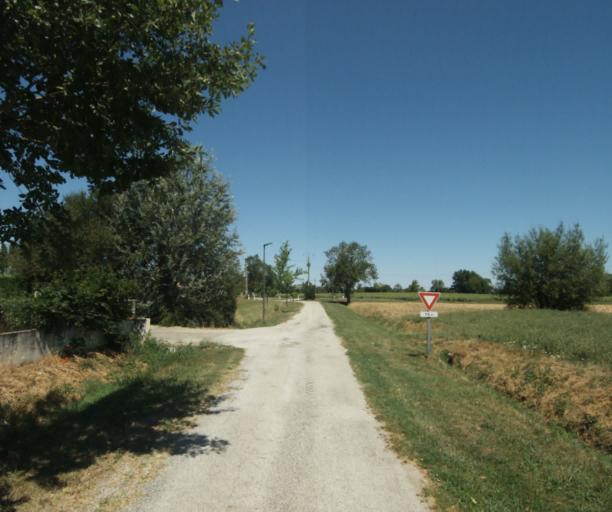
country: FR
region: Midi-Pyrenees
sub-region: Departement de la Haute-Garonne
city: Saint-Felix-Lauragais
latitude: 43.4627
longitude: 1.9331
